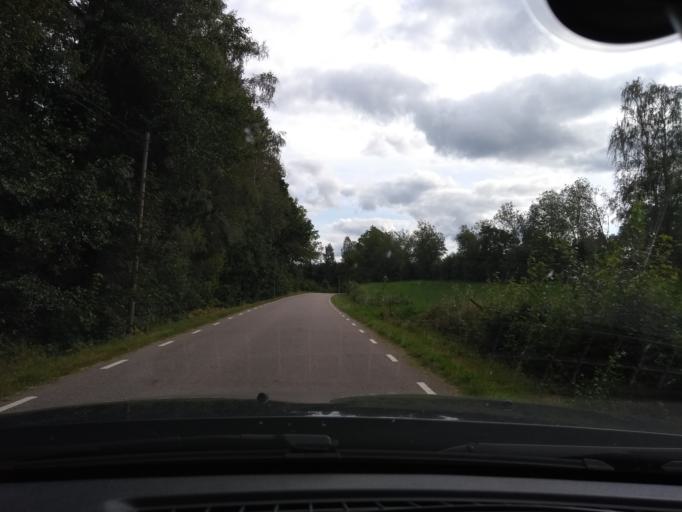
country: SE
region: Joenkoeping
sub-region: Eksjo Kommun
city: Mariannelund
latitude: 57.6236
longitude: 15.7085
